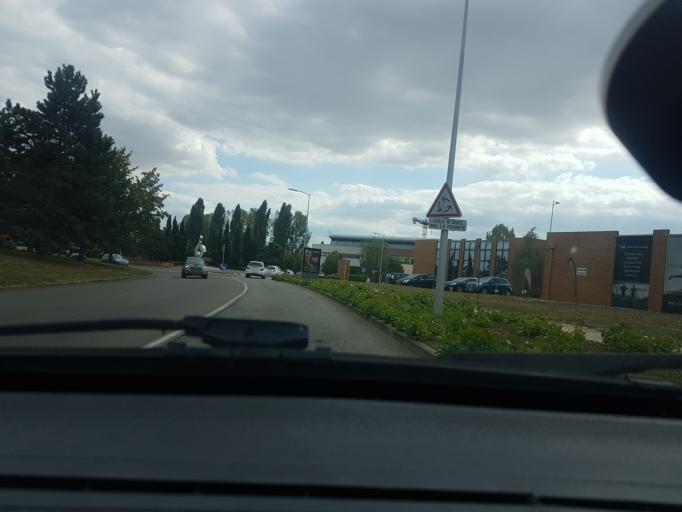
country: FR
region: Bourgogne
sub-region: Departement de la Cote-d'Or
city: Quetigny
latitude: 47.3110
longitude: 5.0936
